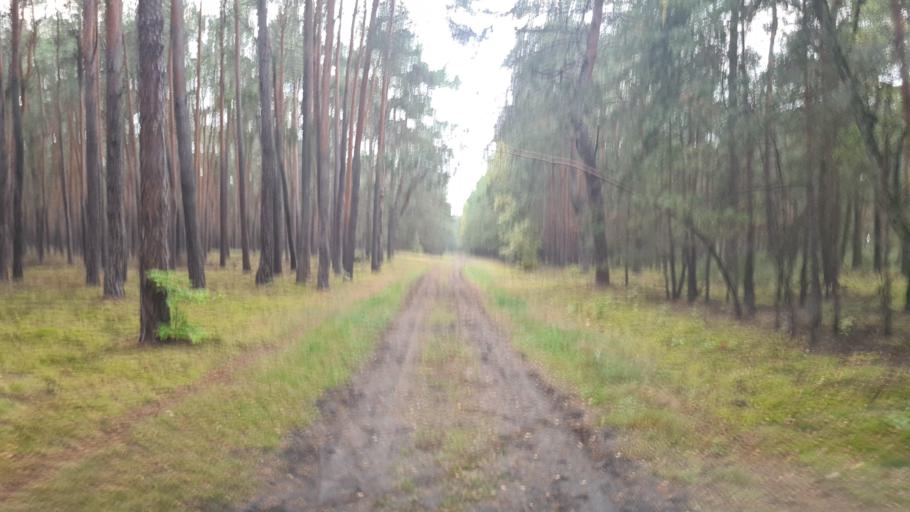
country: DE
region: Brandenburg
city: Storkow
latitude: 52.2243
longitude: 13.9177
